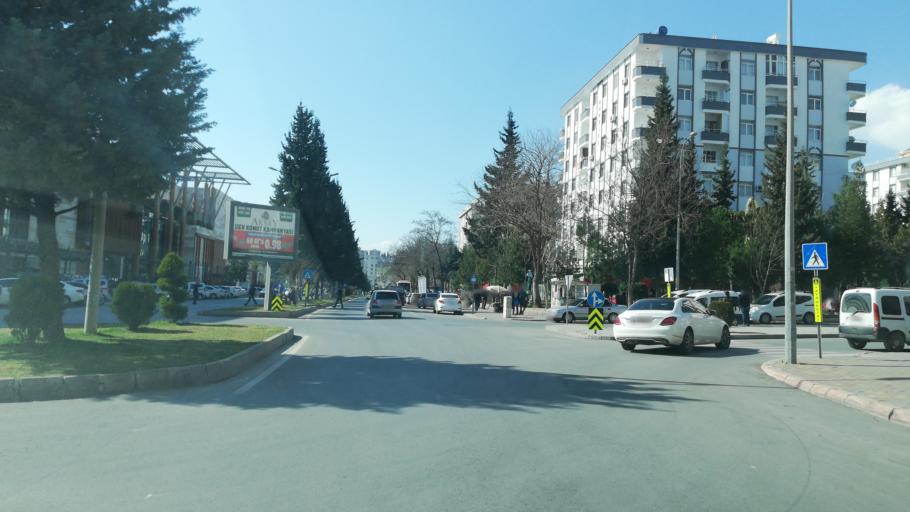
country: TR
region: Kahramanmaras
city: Kahramanmaras
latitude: 37.5710
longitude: 36.9244
